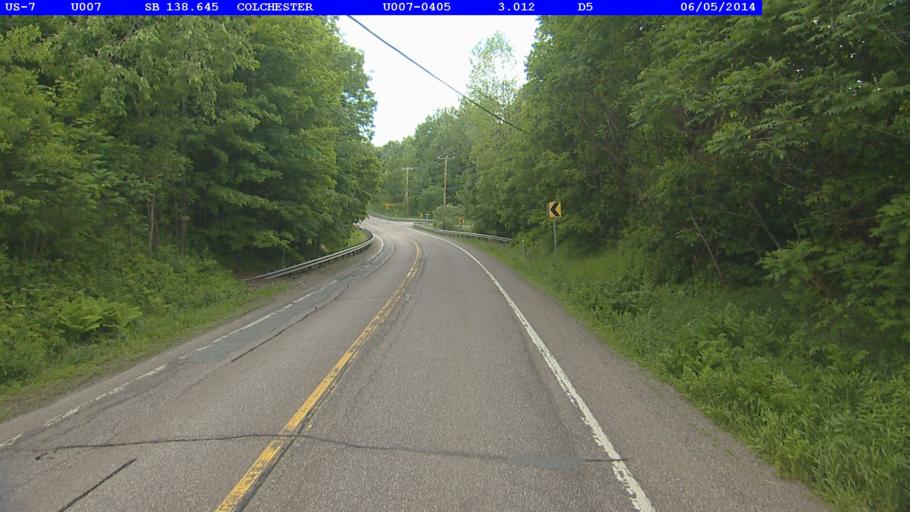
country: US
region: Vermont
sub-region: Chittenden County
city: Colchester
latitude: 44.5427
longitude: -73.1683
